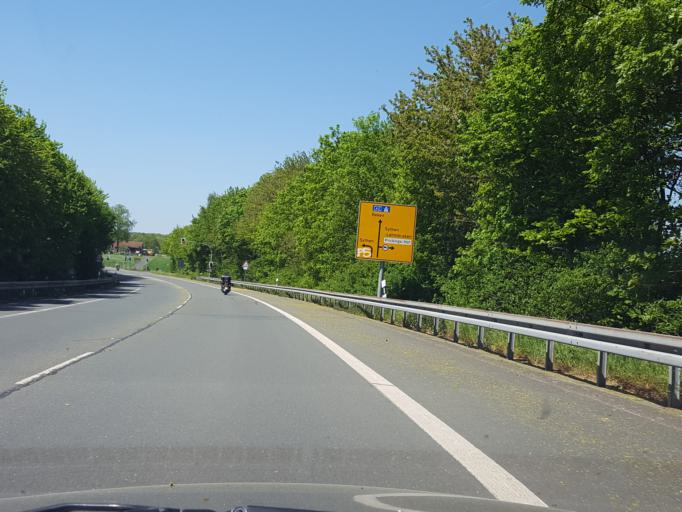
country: DE
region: North Rhine-Westphalia
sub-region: Regierungsbezirk Munster
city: Haltern
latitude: 51.7775
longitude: 7.2301
